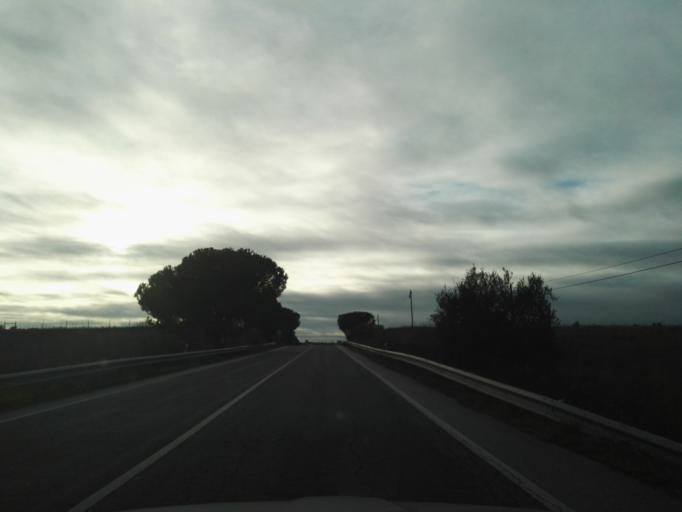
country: PT
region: Evora
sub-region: Redondo
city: Redondo
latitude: 38.6489
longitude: -7.7144
